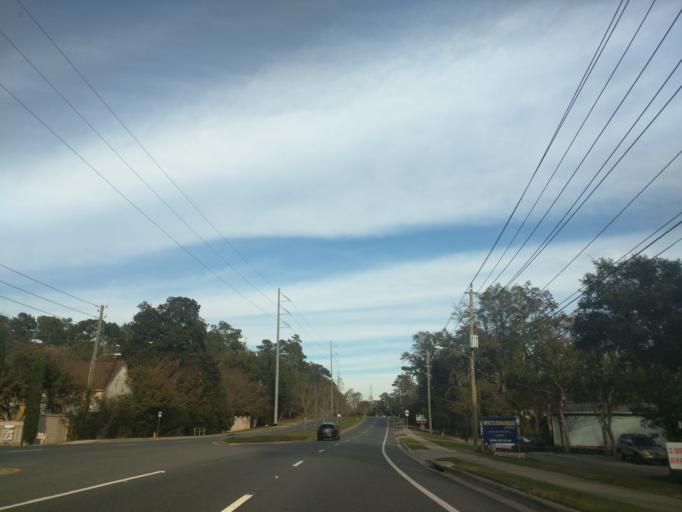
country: US
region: Florida
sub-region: Leon County
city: Tallahassee
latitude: 30.4586
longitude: -84.2517
